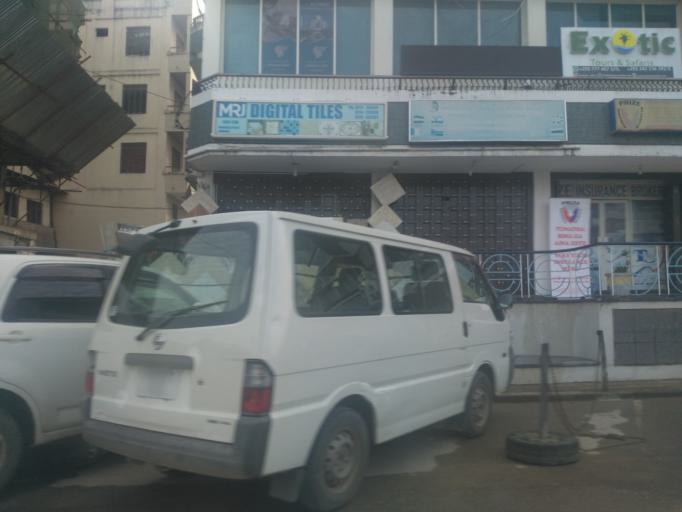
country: TZ
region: Zanzibar Urban/West
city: Zanzibar
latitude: -6.1607
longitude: 39.1990
